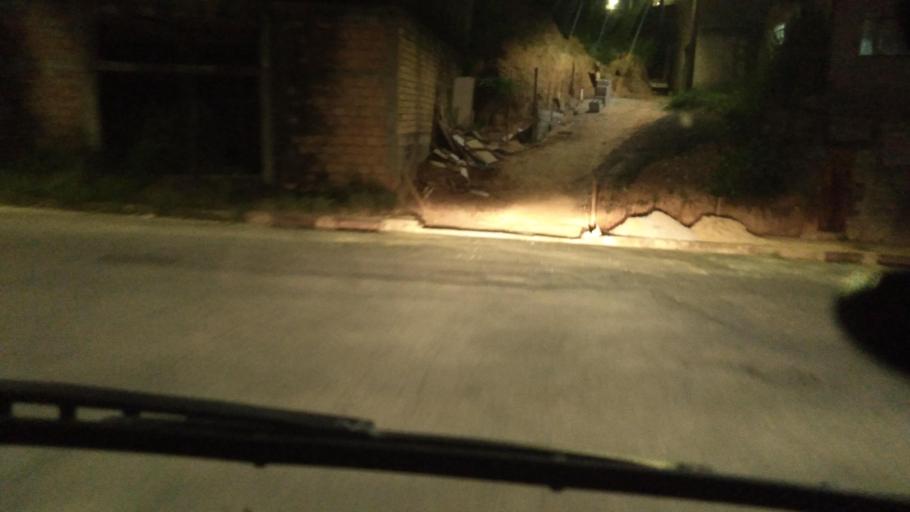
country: BR
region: Minas Gerais
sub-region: Belo Horizonte
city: Belo Horizonte
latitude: -19.9002
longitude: -43.9559
